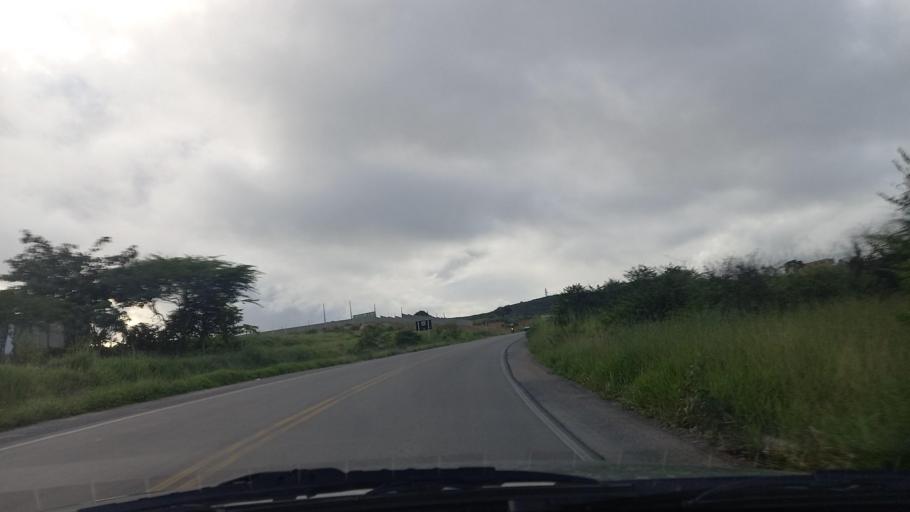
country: BR
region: Pernambuco
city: Garanhuns
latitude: -8.8911
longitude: -36.5060
